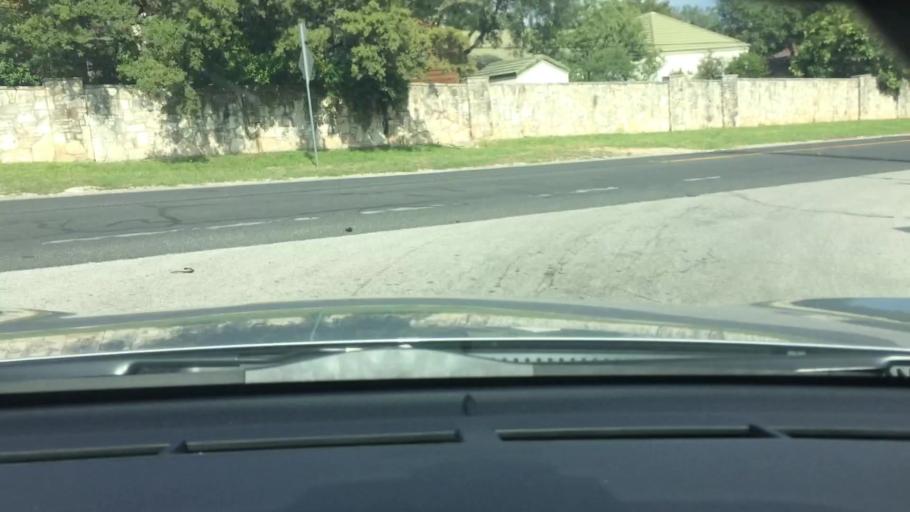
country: US
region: Texas
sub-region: Bexar County
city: Shavano Park
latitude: 29.5616
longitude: -98.5548
